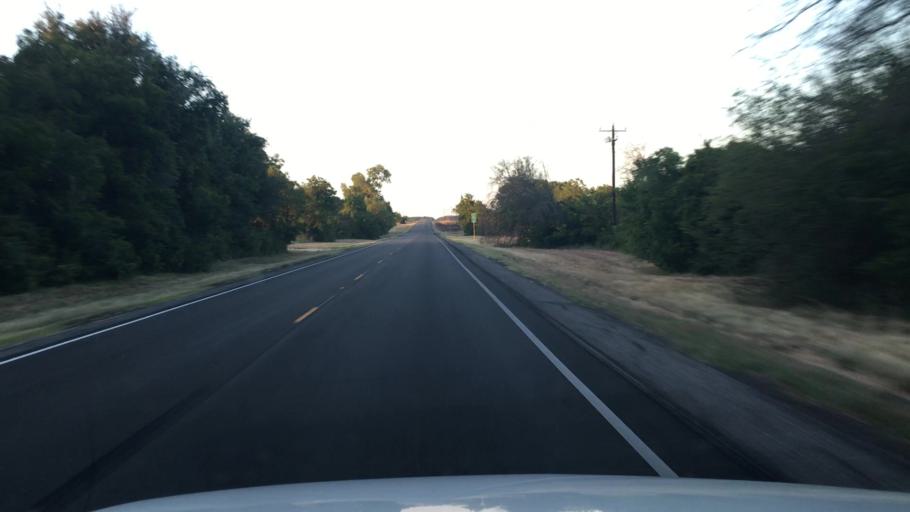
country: US
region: Texas
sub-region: Hamilton County
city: Hico
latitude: 32.0671
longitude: -97.9903
